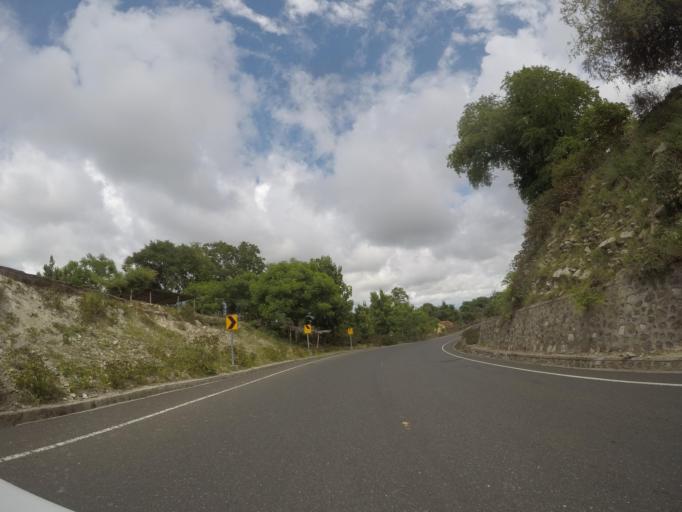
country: TL
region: Liquica
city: Maubara
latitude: -8.7441
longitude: 125.1164
